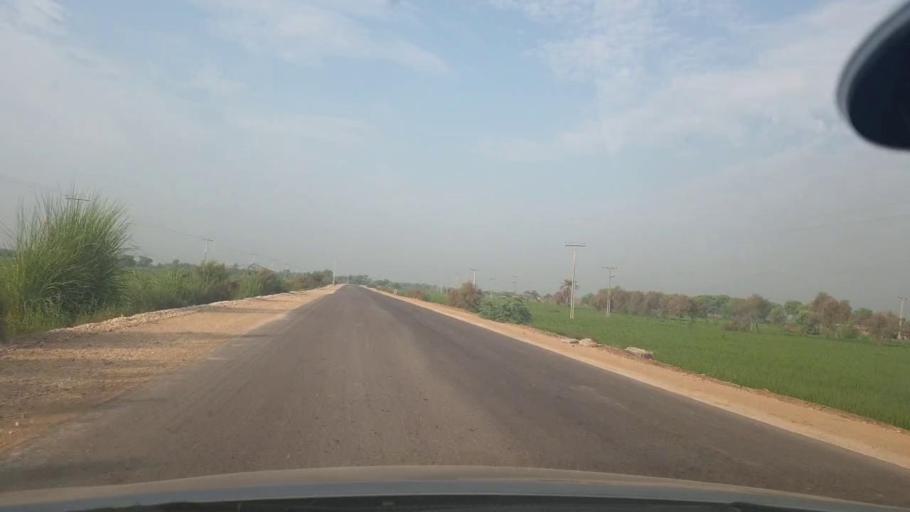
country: PK
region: Sindh
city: Jacobabad
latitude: 28.2501
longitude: 68.4038
